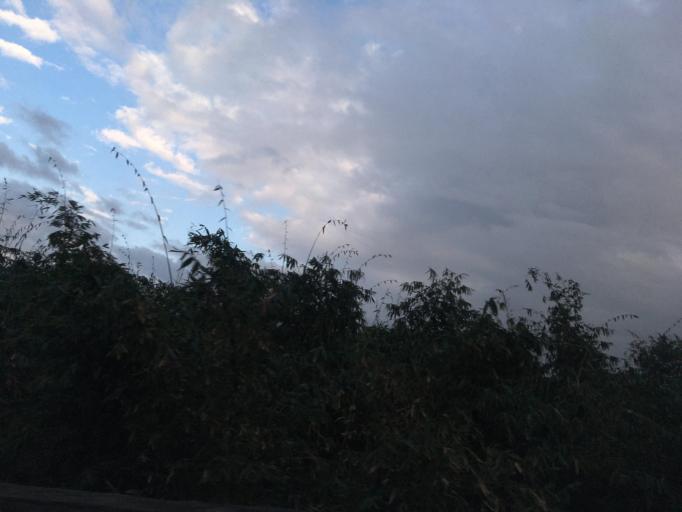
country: TW
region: Taiwan
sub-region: Yilan
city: Yilan
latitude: 24.7535
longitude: 121.7326
